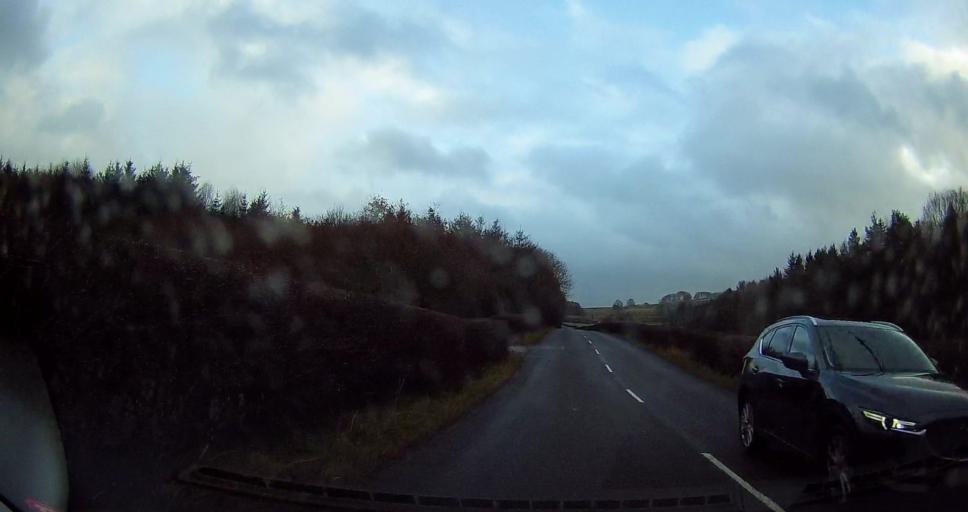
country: GB
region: England
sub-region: Derbyshire
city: Bakewell
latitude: 53.2315
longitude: -1.6697
